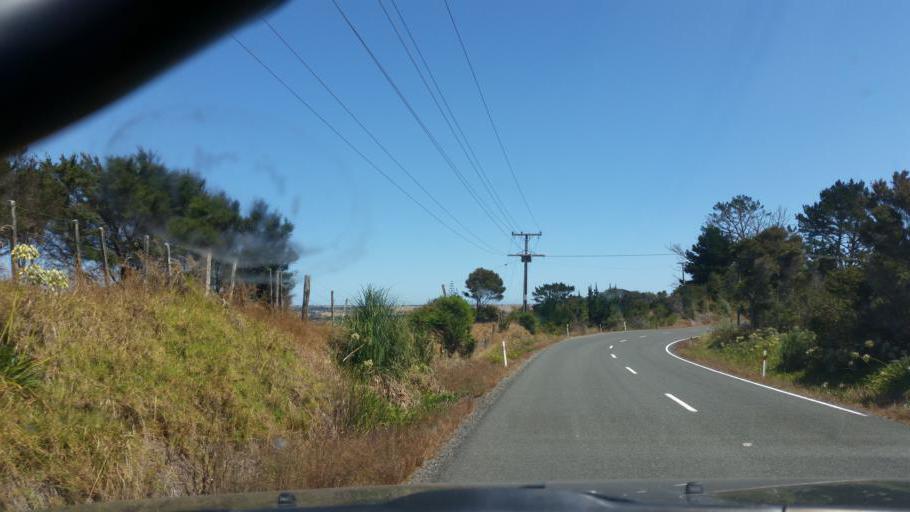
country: NZ
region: Northland
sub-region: Kaipara District
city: Dargaville
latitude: -36.0088
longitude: 173.9444
